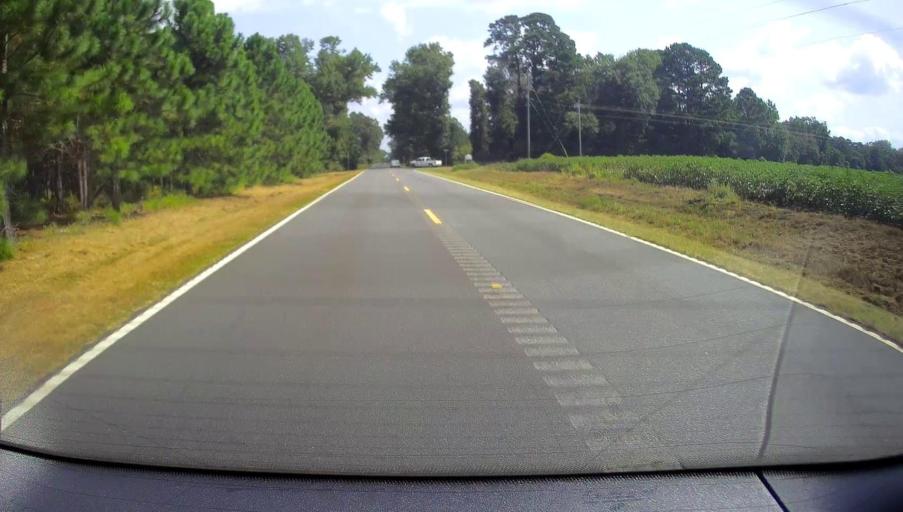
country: US
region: Georgia
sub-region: Bleckley County
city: Cochran
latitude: 32.4917
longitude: -83.3332
